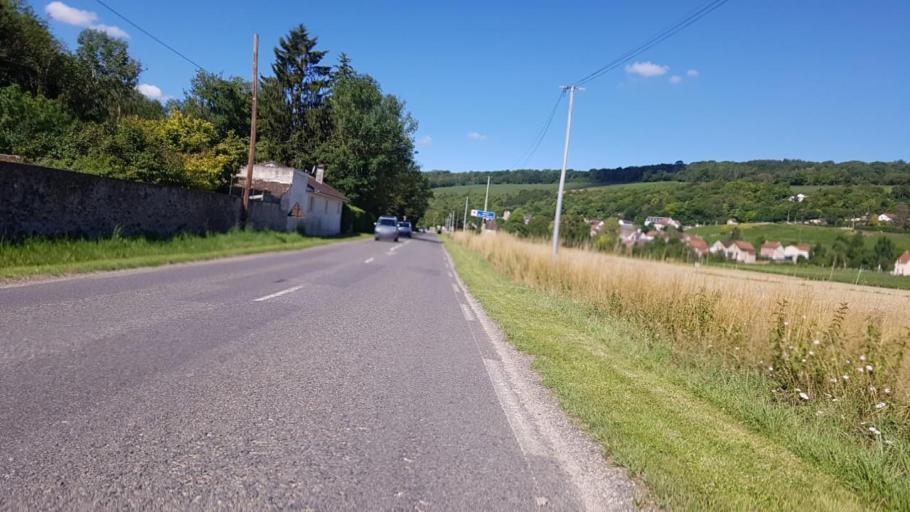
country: FR
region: Ile-de-France
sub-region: Departement de Seine-et-Marne
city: Saacy-sur-Marne
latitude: 48.9780
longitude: 3.2287
